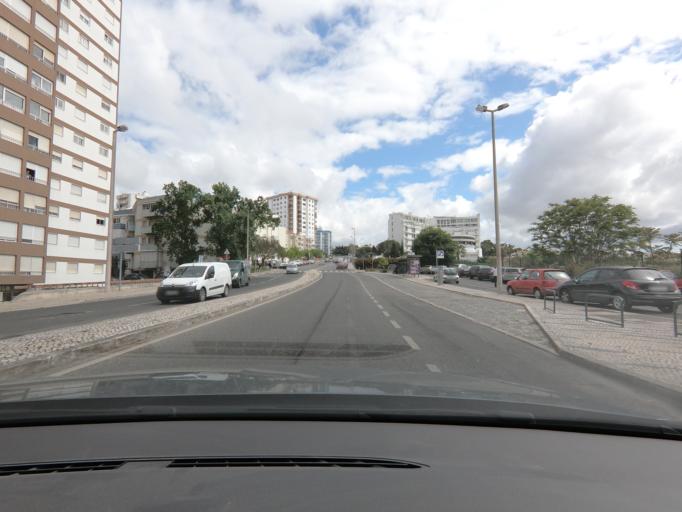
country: PT
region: Lisbon
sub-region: Oeiras
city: Carnaxide
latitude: 38.7252
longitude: -9.2346
